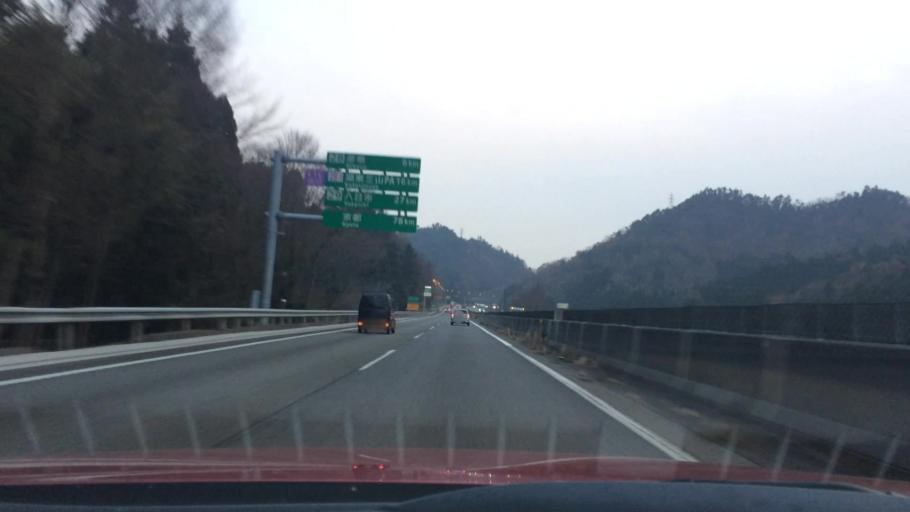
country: JP
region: Shiga Prefecture
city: Hikone
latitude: 35.3052
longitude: 136.3094
